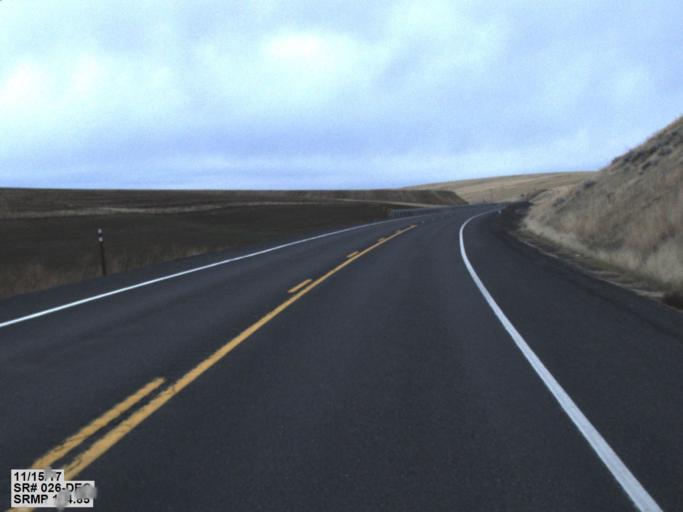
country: US
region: Washington
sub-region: Whitman County
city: Colfax
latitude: 46.8089
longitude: -117.6953
